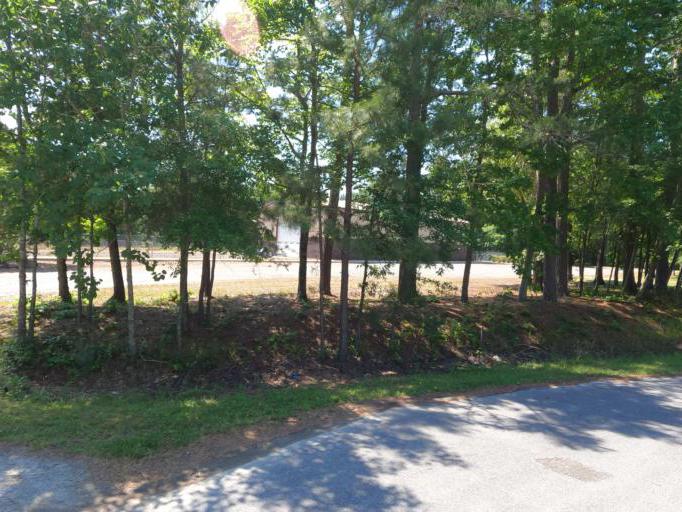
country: US
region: Delaware
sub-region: Sussex County
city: Georgetown
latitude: 38.6956
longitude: -75.3504
